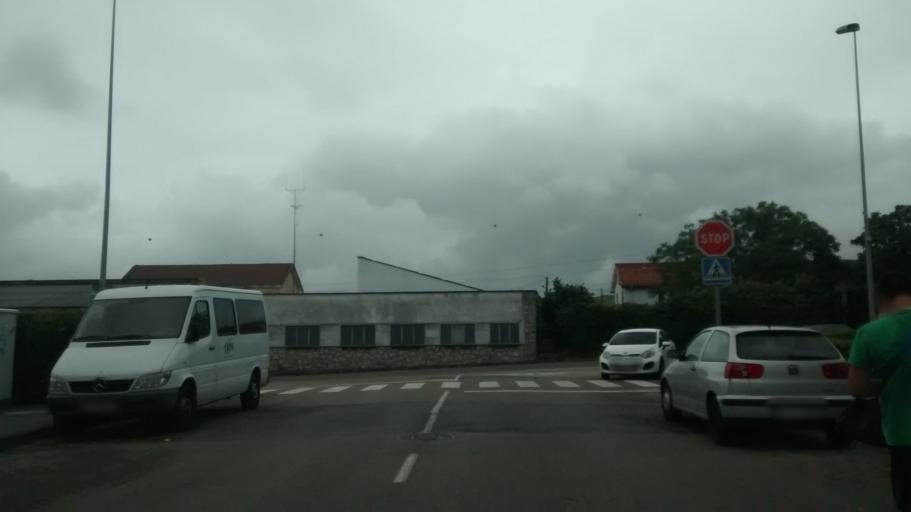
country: ES
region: Cantabria
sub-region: Provincia de Cantabria
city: Camargo
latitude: 43.4401
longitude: -3.8631
